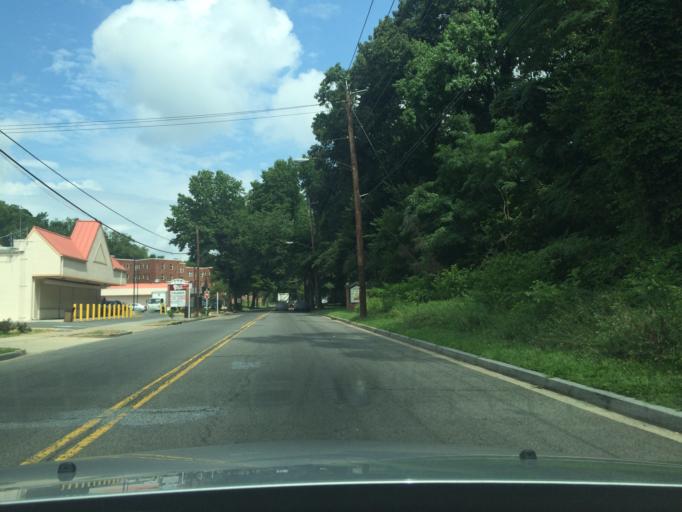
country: US
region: Maryland
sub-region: Prince George's County
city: Hillcrest Heights
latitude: 38.8531
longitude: -76.9638
